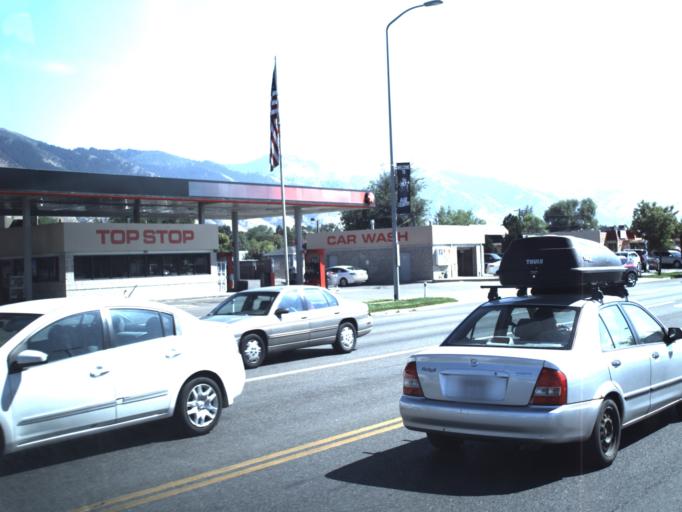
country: US
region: Utah
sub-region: Cache County
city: Logan
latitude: 41.7500
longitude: -111.8346
